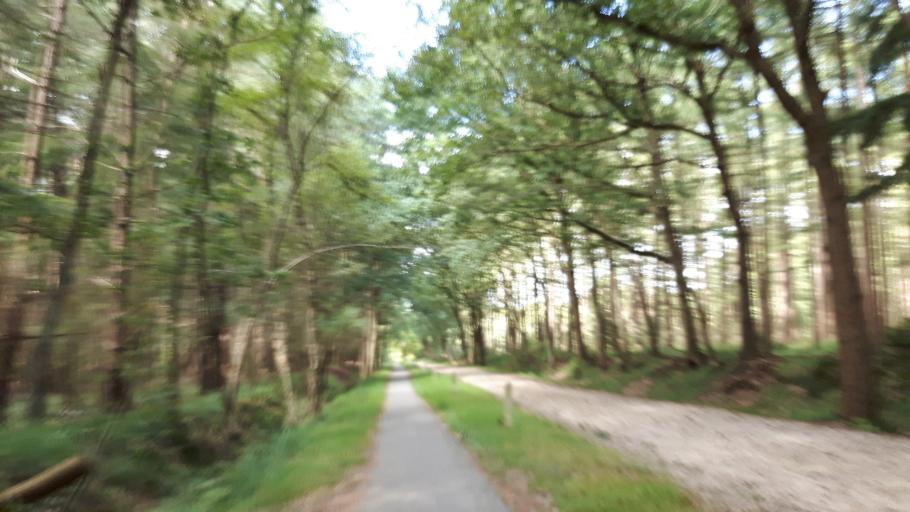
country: NL
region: Friesland
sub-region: Gemeente Smallingerland
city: Drachtstercompagnie
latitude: 53.0812
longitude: 6.2366
